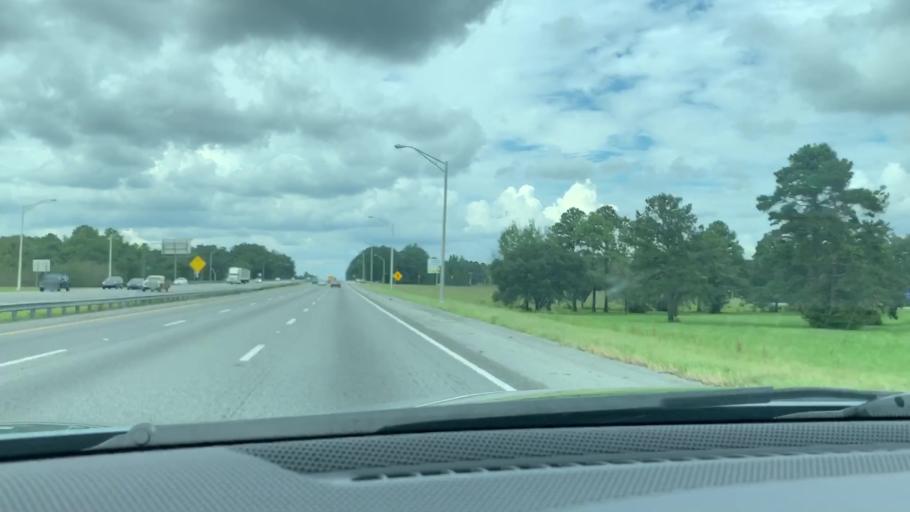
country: US
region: Georgia
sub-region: Bryan County
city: Richmond Hill
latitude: 31.9249
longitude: -81.3299
